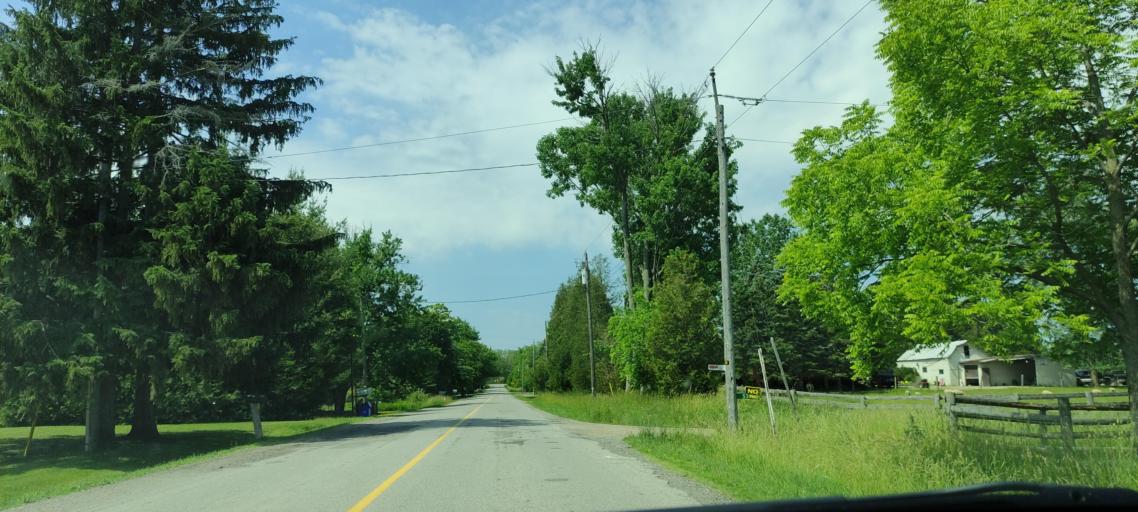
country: CA
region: Ontario
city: Burlington
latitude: 43.3573
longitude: -79.9699
